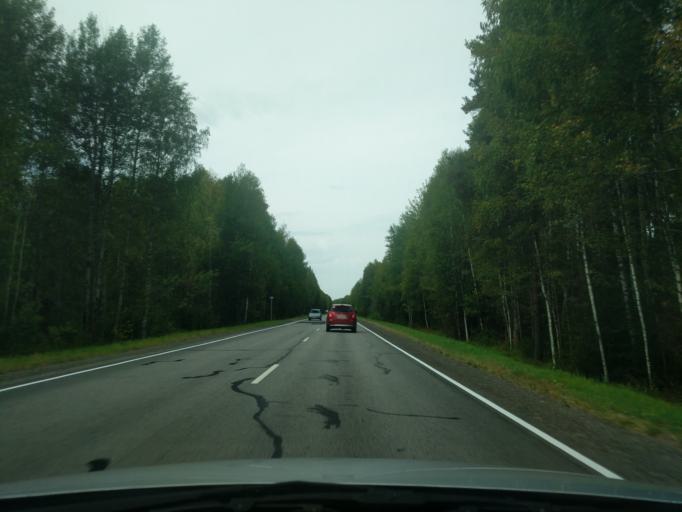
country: RU
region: Kirov
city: Kotel'nich
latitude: 58.2710
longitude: 48.0910
